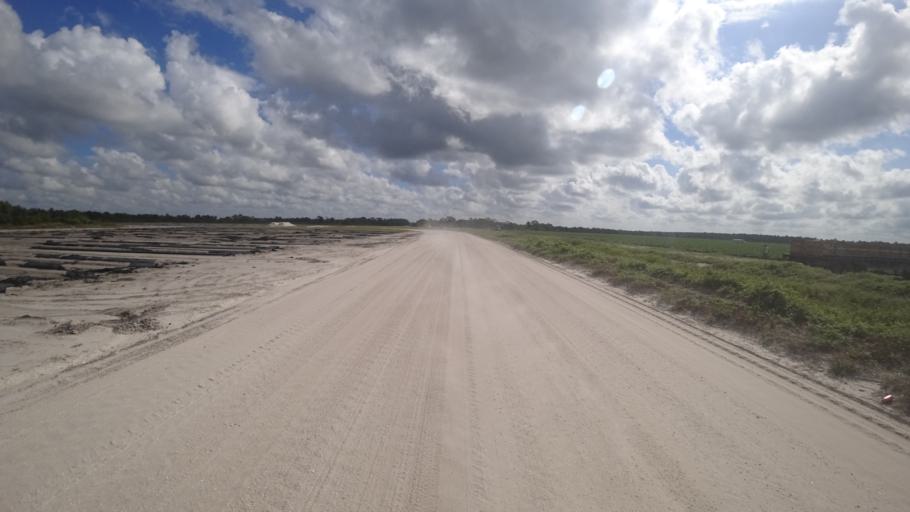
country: US
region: Florida
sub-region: Sarasota County
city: Lake Sarasota
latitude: 27.4129
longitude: -82.2035
